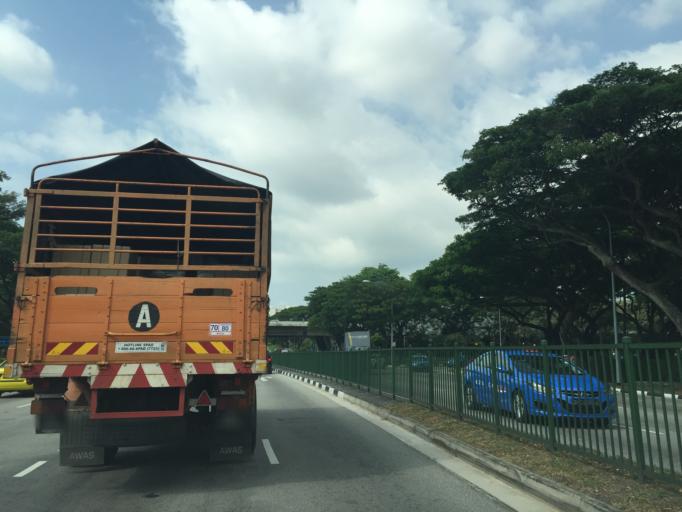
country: SG
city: Singapore
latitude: 1.3241
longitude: 103.8909
